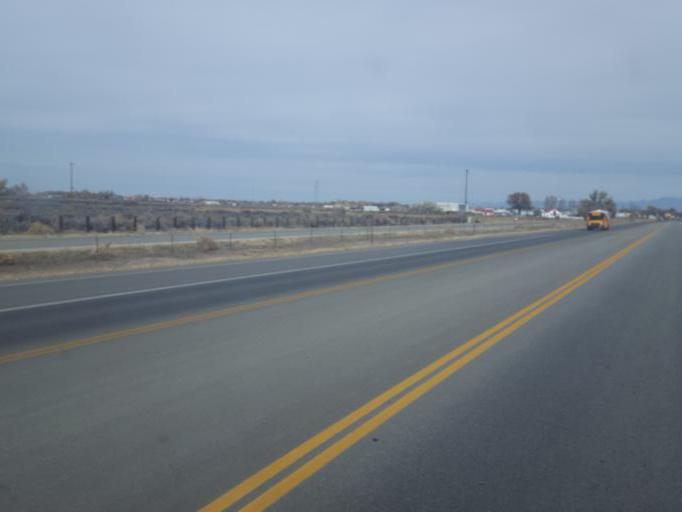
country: US
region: Colorado
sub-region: Alamosa County
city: Alamosa
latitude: 37.4521
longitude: -105.8791
